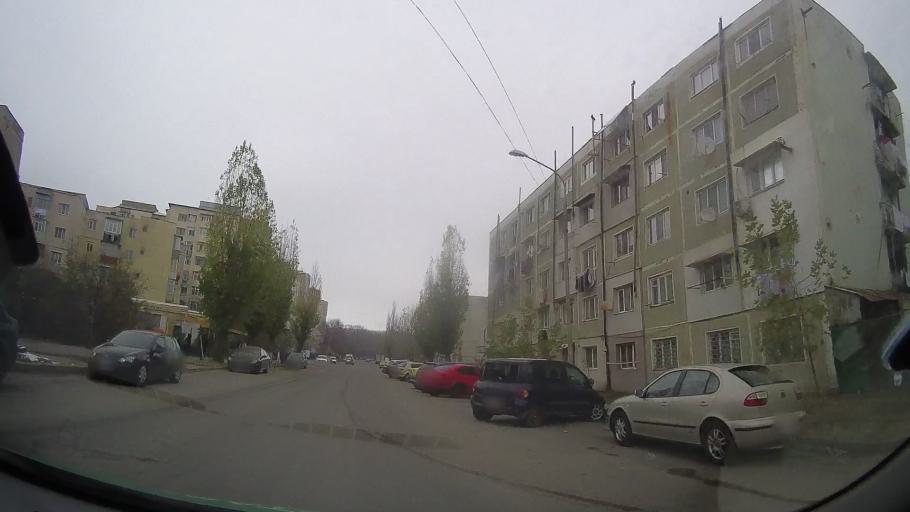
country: RO
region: Vaslui
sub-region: Municipiul Barlad
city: Barlad
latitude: 46.2385
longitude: 27.6771
